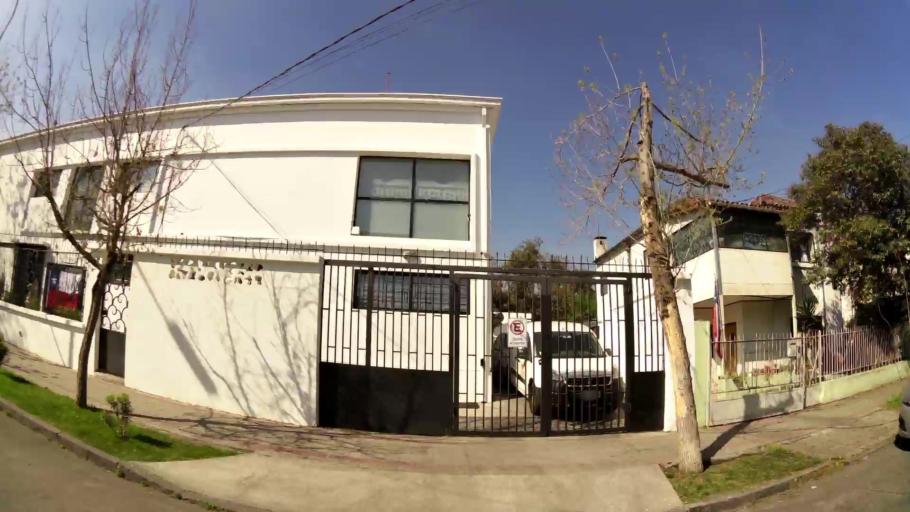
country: CL
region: Santiago Metropolitan
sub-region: Provincia de Santiago
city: Santiago
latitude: -33.4446
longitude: -70.6247
